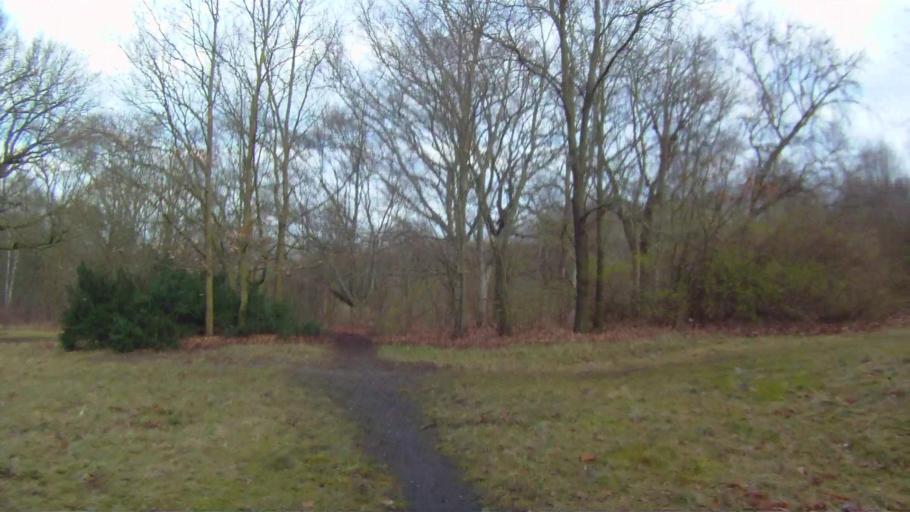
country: DE
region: Berlin
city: Oberschoneweide
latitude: 52.4655
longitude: 13.5252
